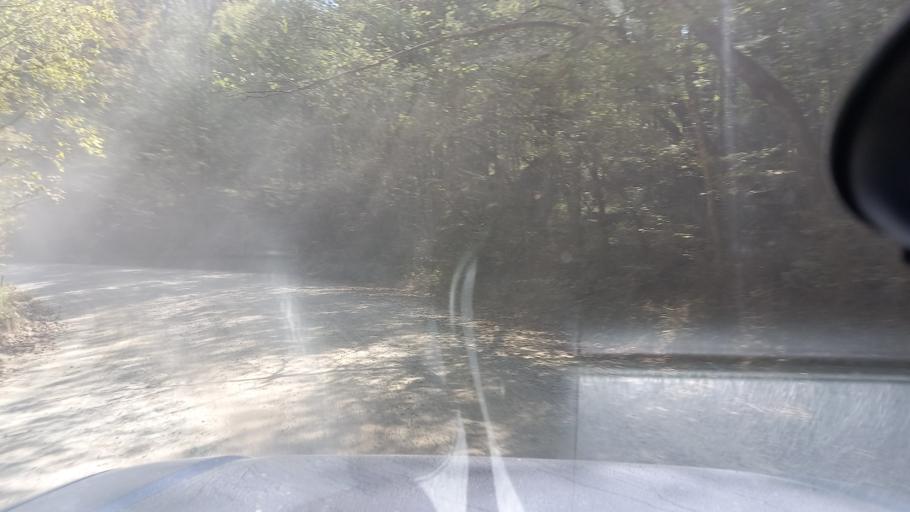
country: RU
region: Krasnodarskiy
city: Azovskaya
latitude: 44.6771
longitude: 38.6336
